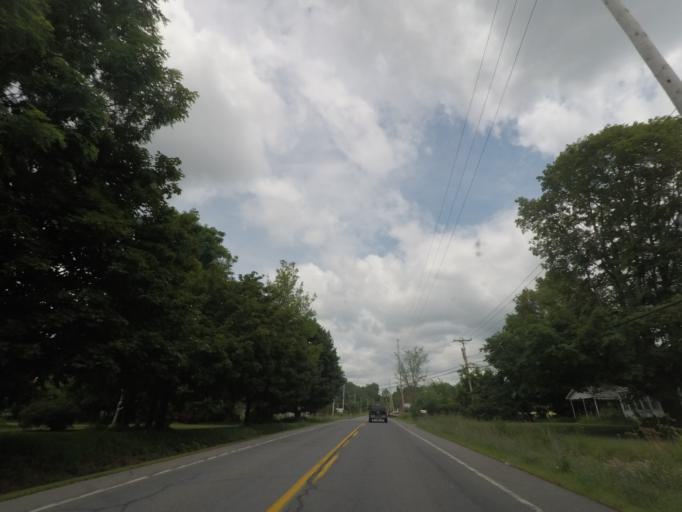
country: US
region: New York
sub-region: Saratoga County
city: Stillwater
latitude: 42.9102
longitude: -73.6231
